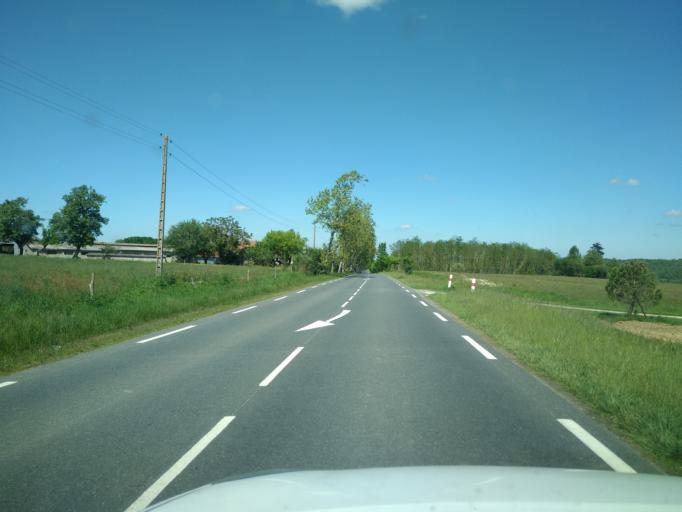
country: FR
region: Midi-Pyrenees
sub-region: Departement de la Haute-Garonne
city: Boulogne-sur-Gesse
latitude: 43.2970
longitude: 0.6683
